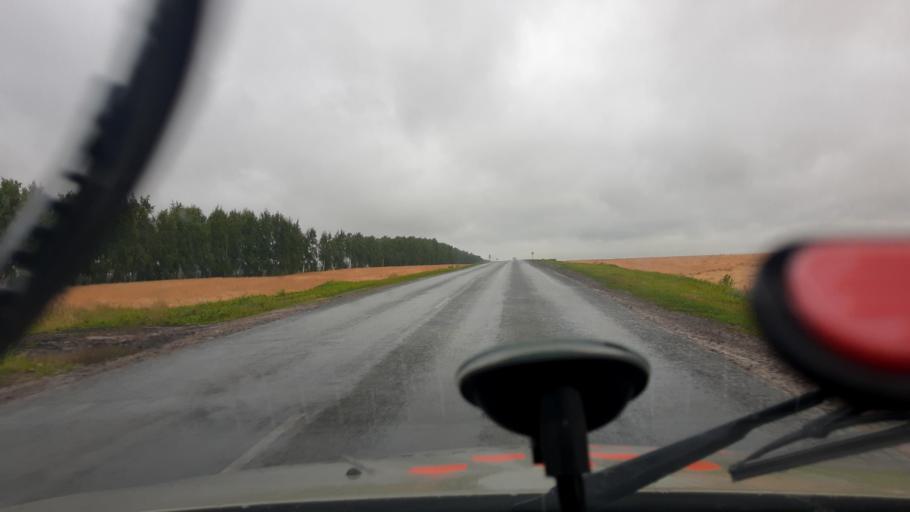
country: RU
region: Bashkortostan
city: Chekmagush
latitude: 55.0731
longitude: 54.6330
